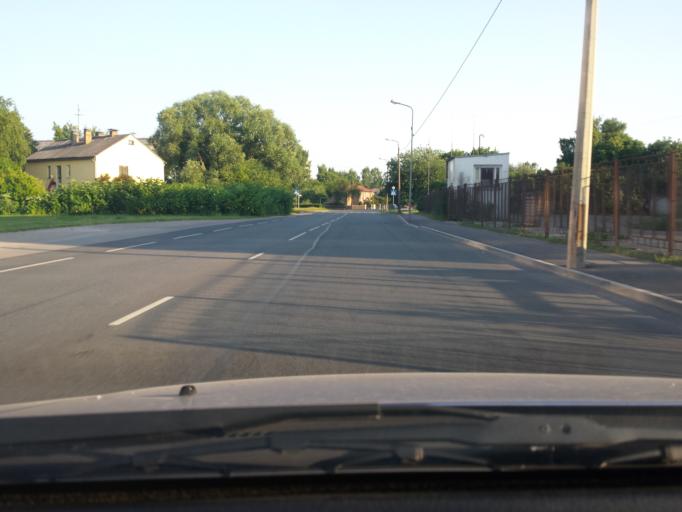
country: LV
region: Riga
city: Riga
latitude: 56.9574
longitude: 24.1656
